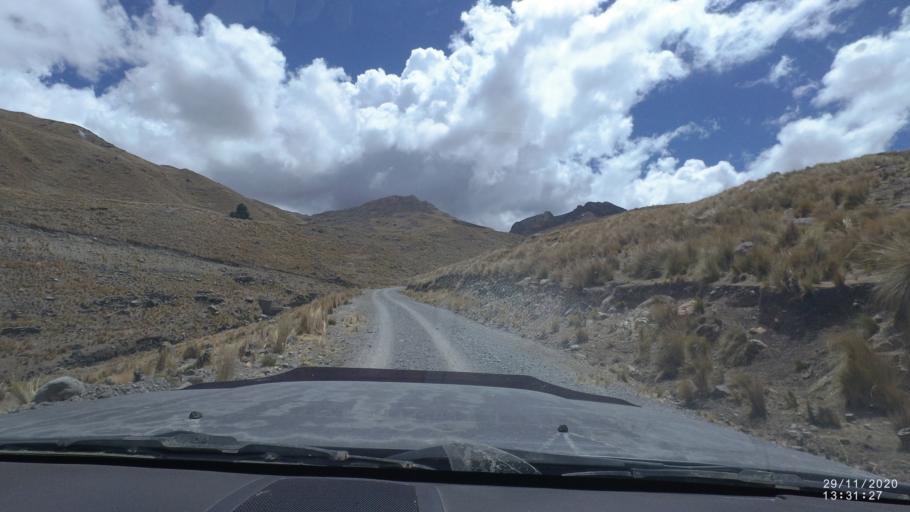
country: BO
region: Cochabamba
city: Cochabamba
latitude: -17.1055
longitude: -66.3437
